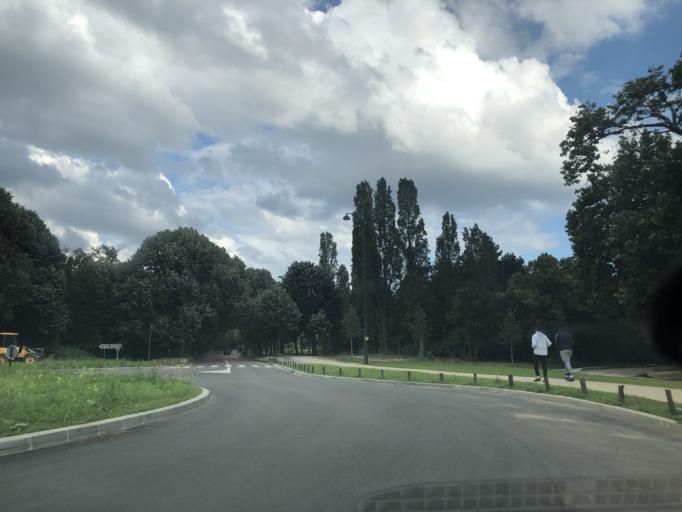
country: FR
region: Ile-de-France
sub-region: Departement du Val-de-Marne
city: Vincennes
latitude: 48.8340
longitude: 2.4449
